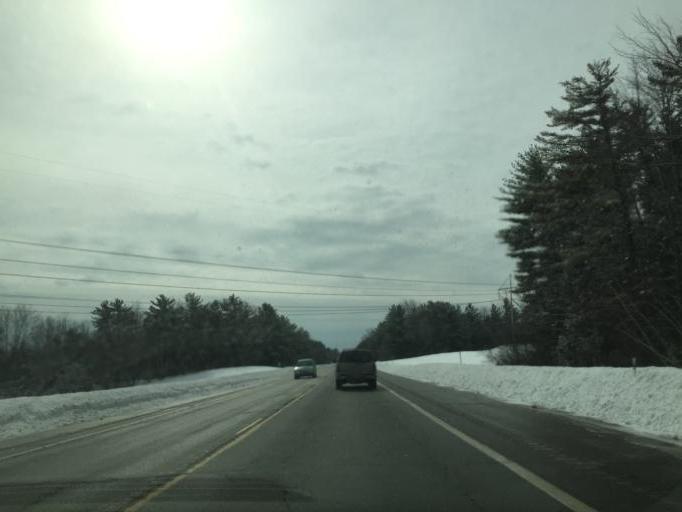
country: US
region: New Hampshire
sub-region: Strafford County
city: Rochester
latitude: 43.3501
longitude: -70.9855
